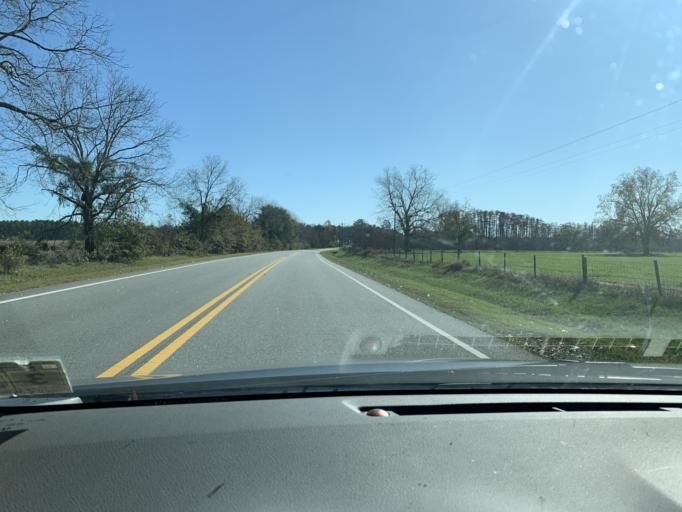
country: US
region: Georgia
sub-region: Ben Hill County
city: Fitzgerald
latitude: 31.7140
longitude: -83.1733
